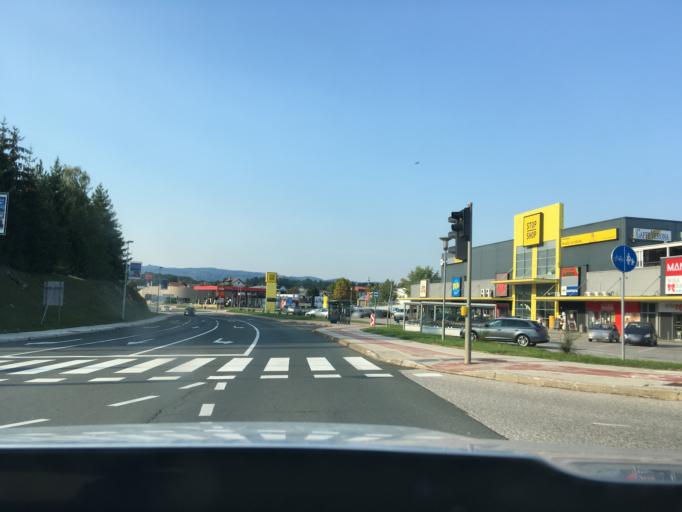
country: SI
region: Novo Mesto
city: Novo Mesto
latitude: 45.7960
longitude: 15.1810
